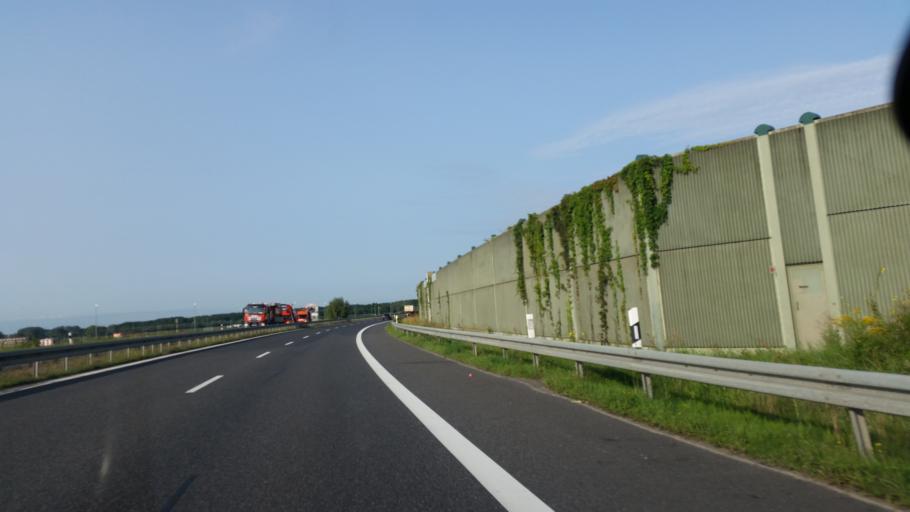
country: DE
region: Brandenburg
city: Schonefeld
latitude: 52.3701
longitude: 13.4809
